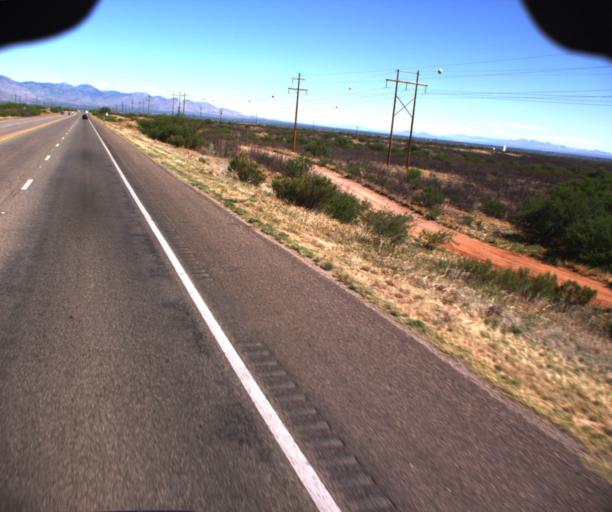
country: US
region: Arizona
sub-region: Cochise County
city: Sierra Vista
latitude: 31.5882
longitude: -110.3217
